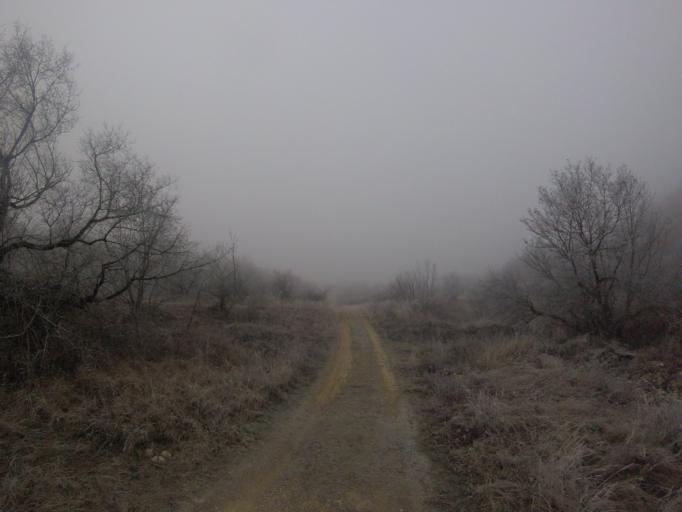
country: HU
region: Fejer
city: Csakvar
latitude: 47.3804
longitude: 18.4373
